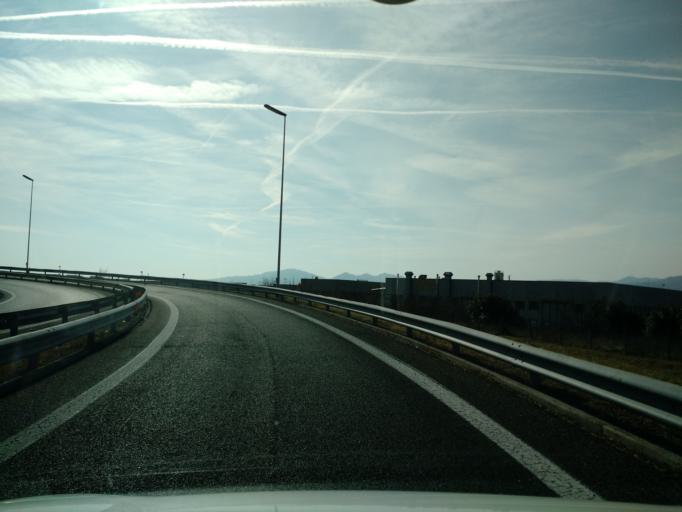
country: IT
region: Veneto
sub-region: Provincia di Vicenza
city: Marano Vicentino
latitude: 45.6830
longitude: 11.4588
